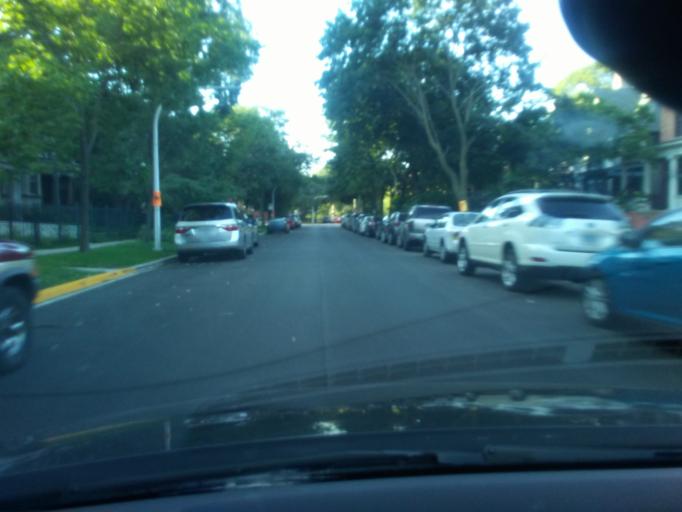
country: US
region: Illinois
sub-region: Cook County
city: Lincolnwood
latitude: 41.9645
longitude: -87.6653
